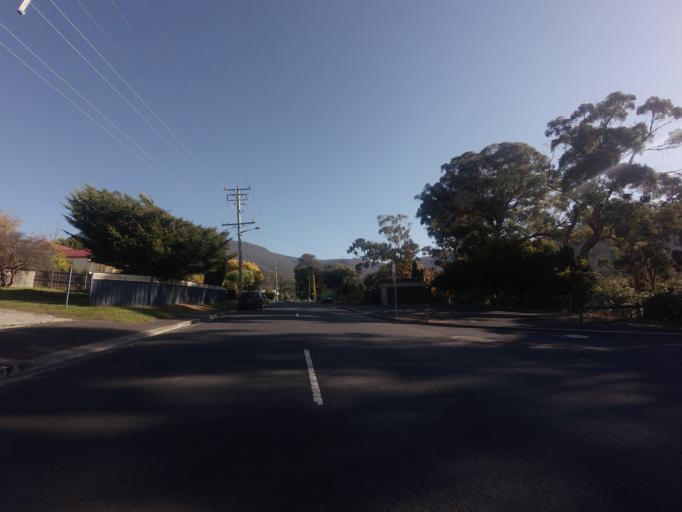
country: AU
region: Tasmania
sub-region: Glenorchy
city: West Moonah
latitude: -42.8509
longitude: 147.2565
